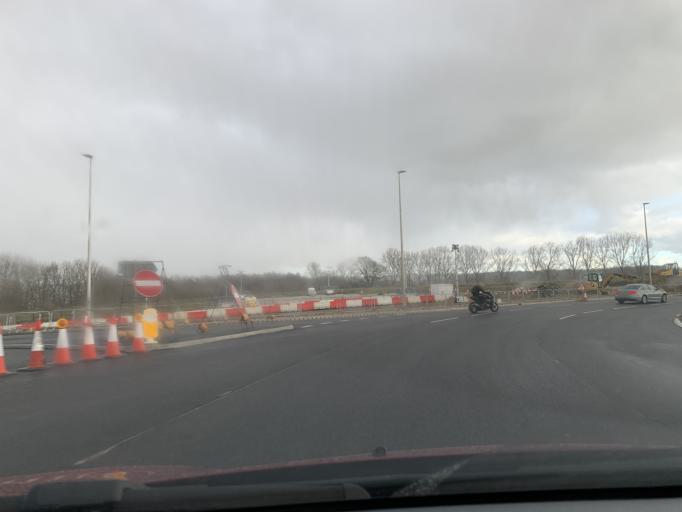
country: GB
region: England
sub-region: Kent
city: Ashford
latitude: 51.1336
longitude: 0.9208
